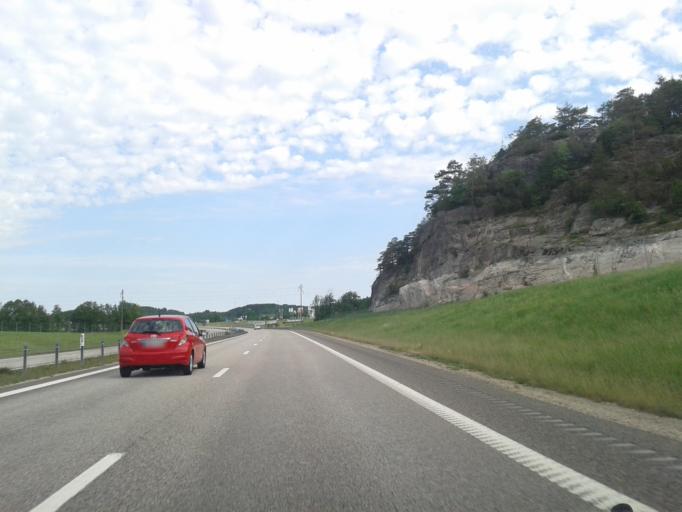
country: SE
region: Vaestra Goetaland
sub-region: Munkedals Kommun
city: Munkedal
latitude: 58.4817
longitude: 11.6327
